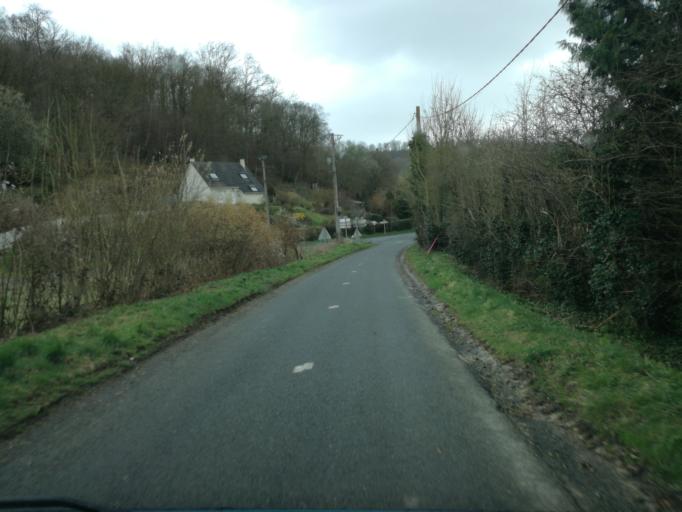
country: FR
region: Haute-Normandie
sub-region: Departement de la Seine-Maritime
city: Saint-Wandrille-Rancon
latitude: 49.5565
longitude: 0.7532
